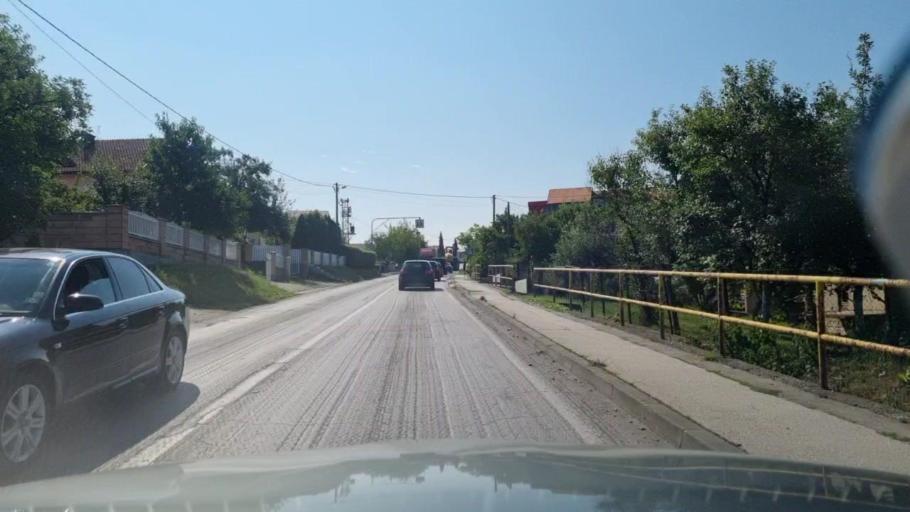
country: BA
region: Federation of Bosnia and Herzegovina
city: Gradacac
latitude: 44.8719
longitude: 18.4287
